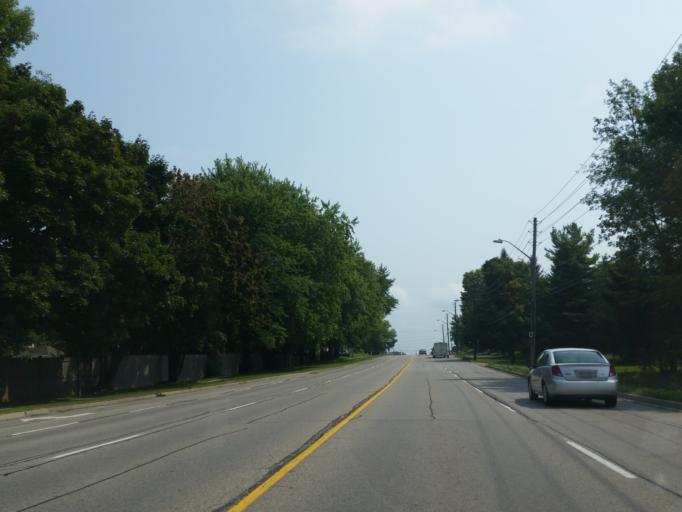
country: CA
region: Ontario
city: Brockville
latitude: 44.6024
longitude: -75.7100
